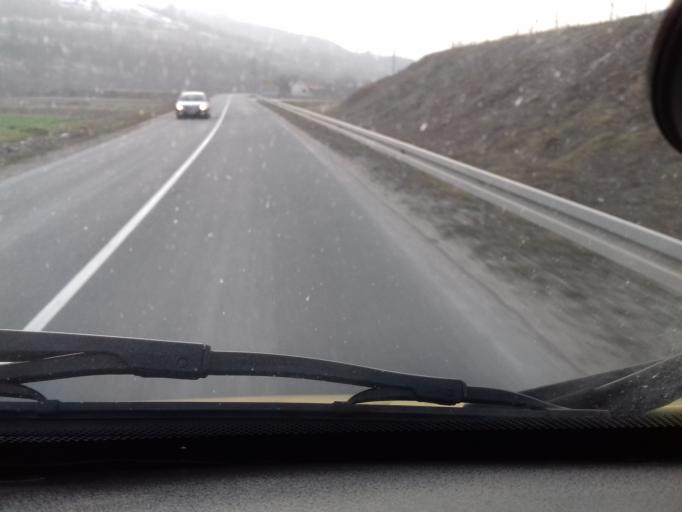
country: BA
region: Federation of Bosnia and Herzegovina
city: Kacuni
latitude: 44.1341
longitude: 18.0029
